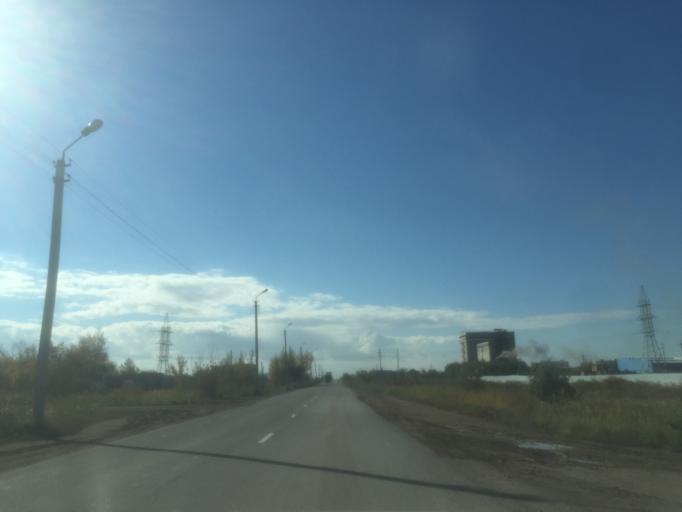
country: KZ
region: Astana Qalasy
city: Astana
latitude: 51.2036
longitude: 71.3508
